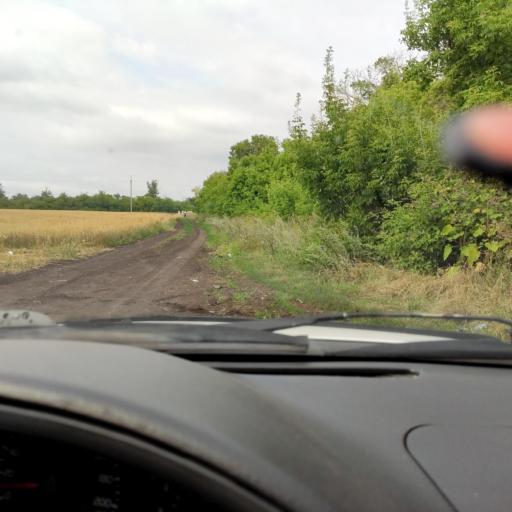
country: RU
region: Bashkortostan
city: Alekseyevka
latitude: 54.7302
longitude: 55.0017
